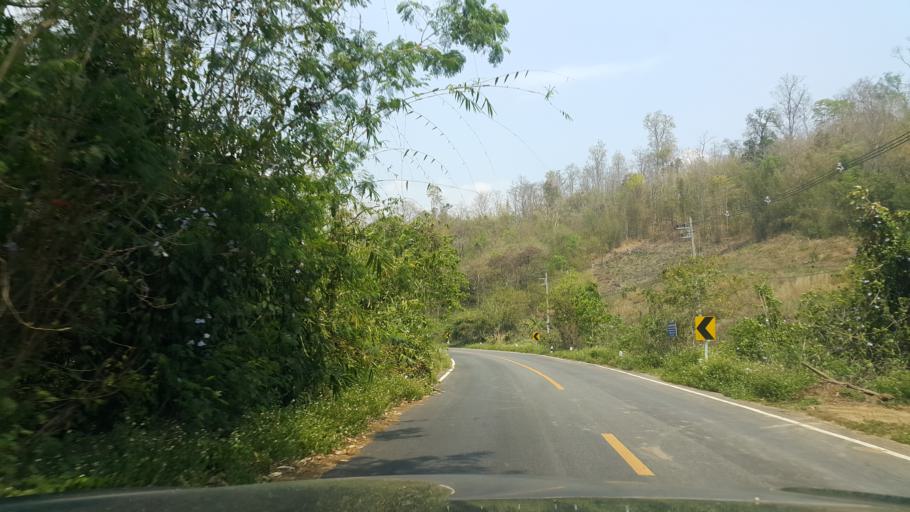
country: TH
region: Lamphun
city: Thung Hua Chang
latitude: 17.9018
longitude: 99.1356
